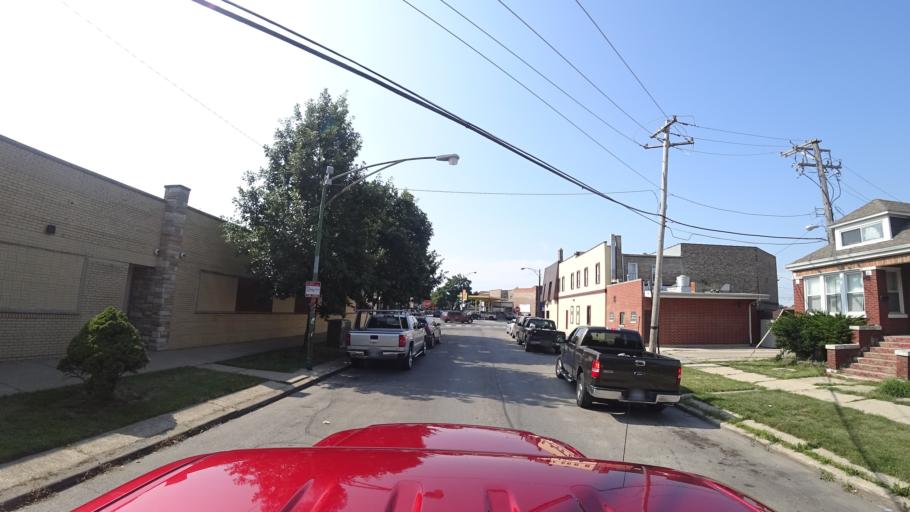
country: US
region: Illinois
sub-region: Cook County
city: Cicero
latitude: 41.8104
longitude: -87.7113
